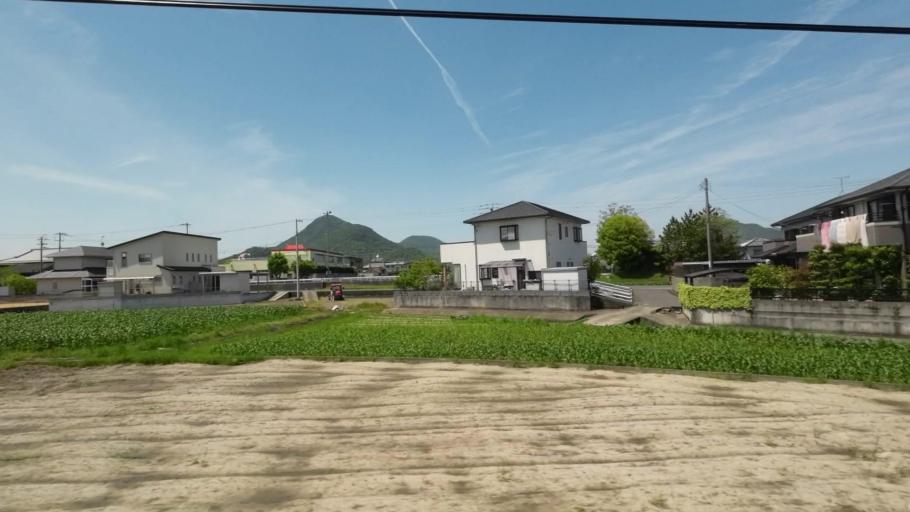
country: JP
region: Kagawa
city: Marugame
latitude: 34.2387
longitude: 133.7840
